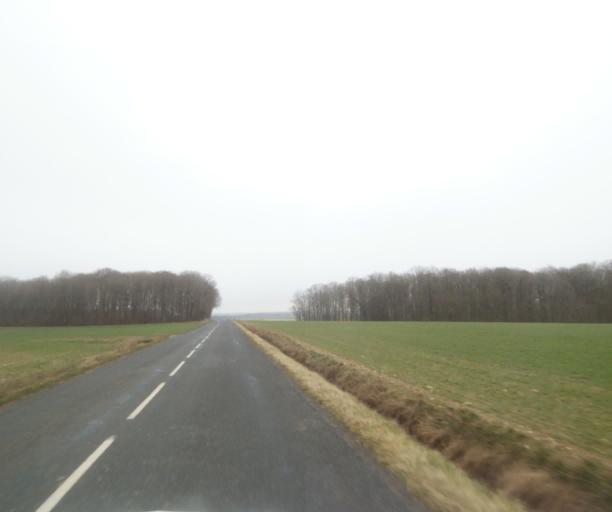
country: FR
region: Champagne-Ardenne
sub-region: Departement de la Haute-Marne
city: Bienville
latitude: 48.5209
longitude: 5.0687
